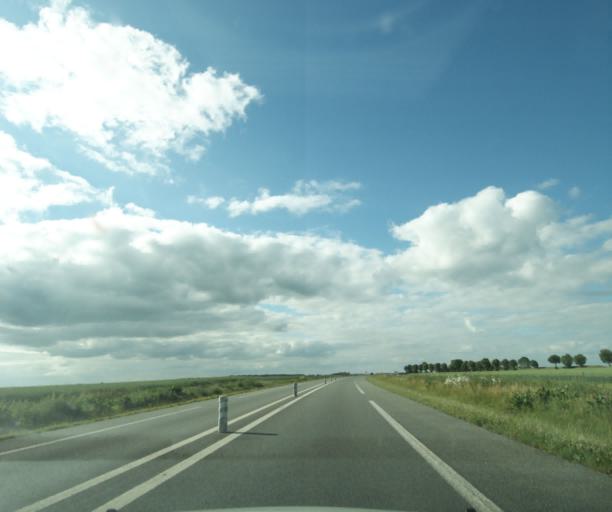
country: FR
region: Centre
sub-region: Departement d'Eure-et-Loir
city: Sours
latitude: 48.3748
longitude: 1.5878
